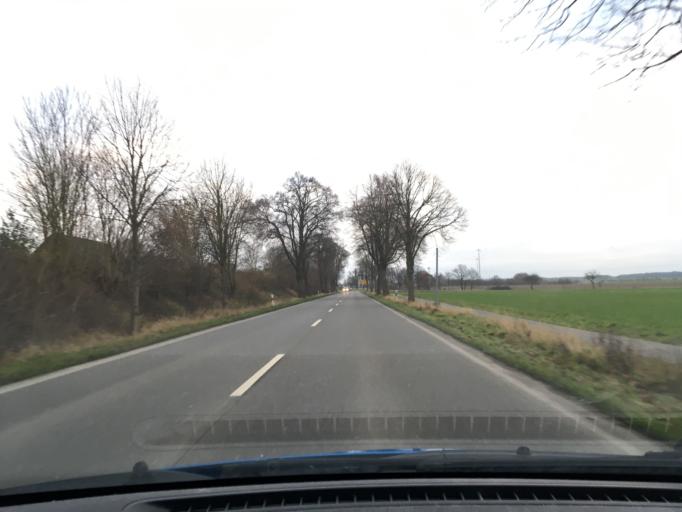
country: DE
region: Lower Saxony
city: Uelzen
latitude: 52.9555
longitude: 10.5801
